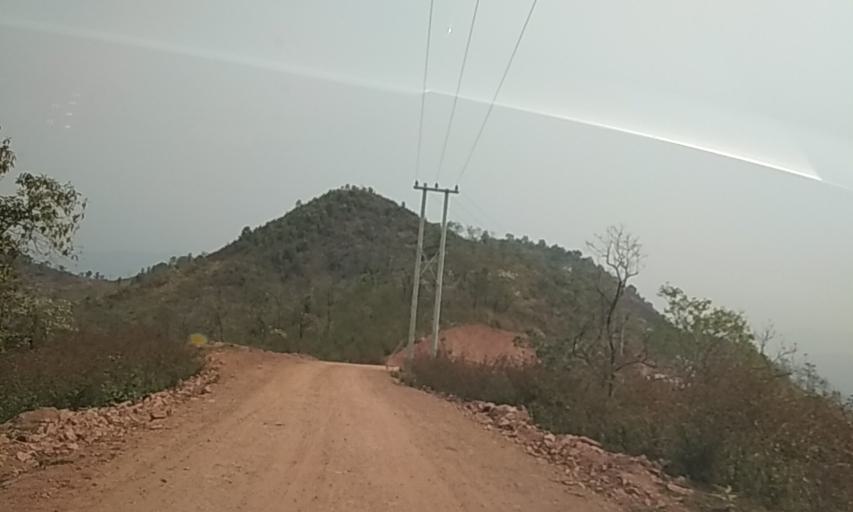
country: VN
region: Huyen Dien Bien
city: Dien Bien Phu
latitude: 21.5054
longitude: 102.7947
